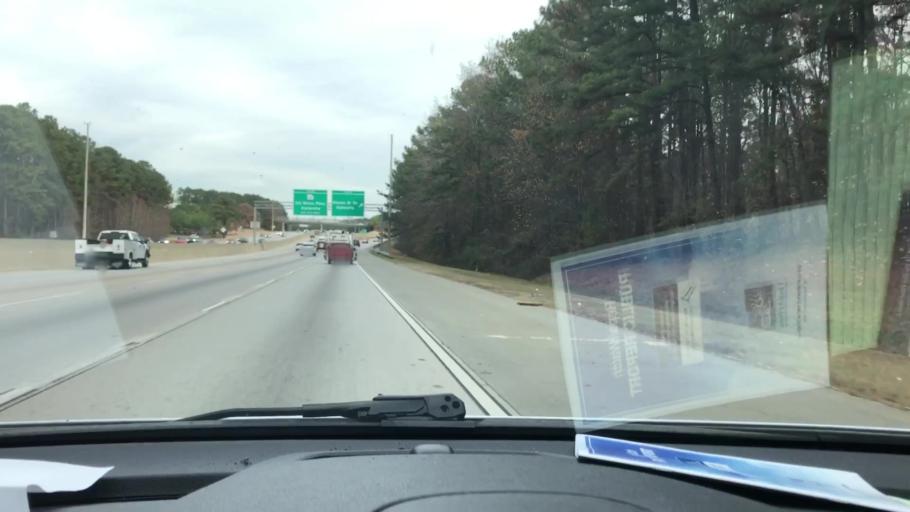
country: US
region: Georgia
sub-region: Fulton County
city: Alpharetta
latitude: 34.0524
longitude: -84.2922
